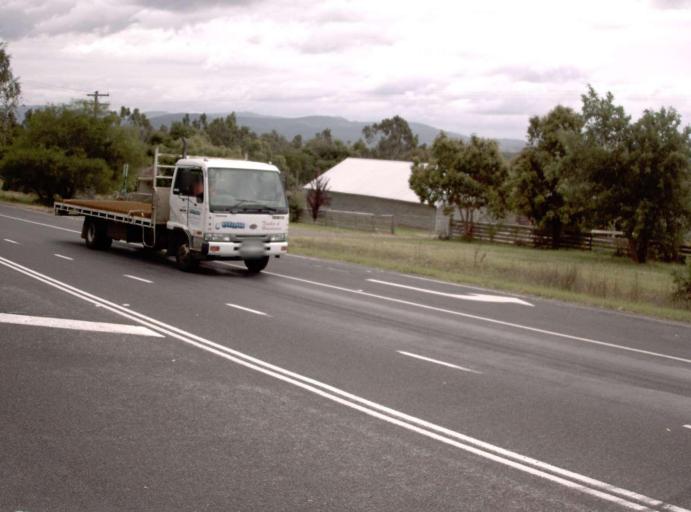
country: AU
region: Victoria
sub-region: Baw Baw
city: Warragul
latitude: -38.0973
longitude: 145.8372
